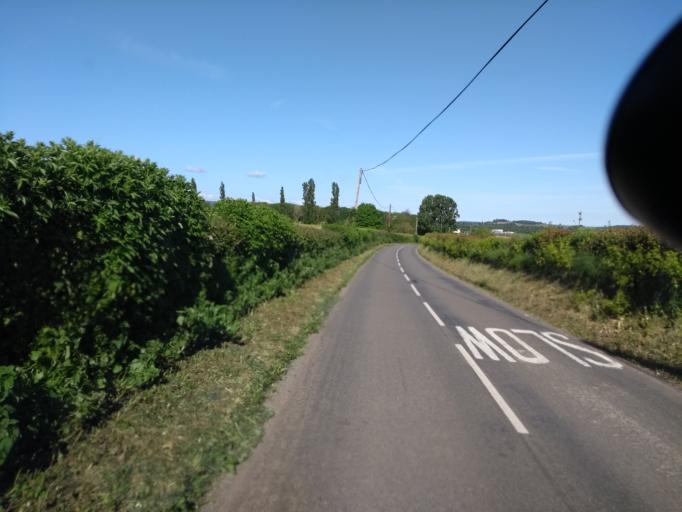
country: GB
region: England
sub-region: Somerset
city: Bridgwater
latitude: 51.1366
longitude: -3.0401
